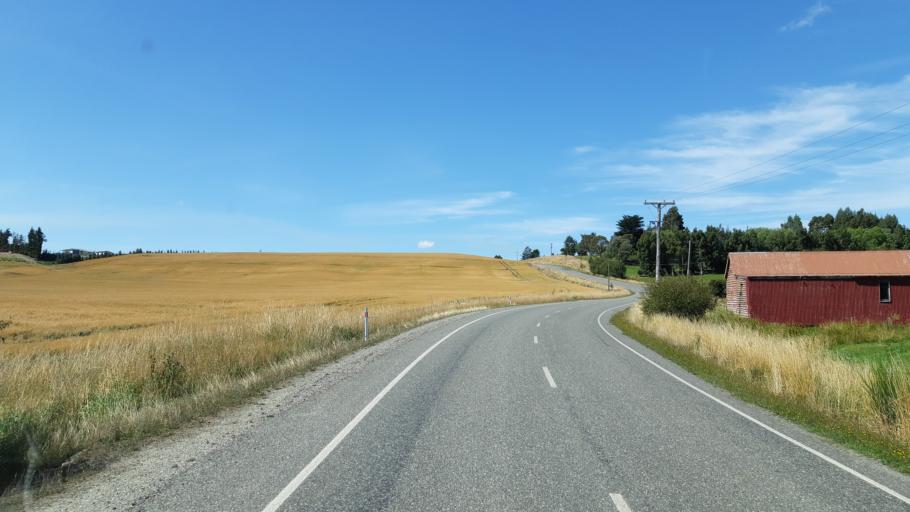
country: NZ
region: Southland
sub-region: Gore District
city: Gore
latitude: -46.0042
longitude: 168.8938
